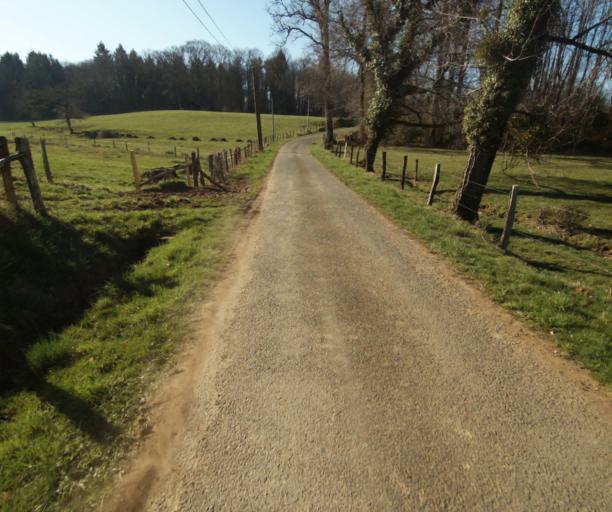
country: FR
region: Limousin
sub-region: Departement de la Correze
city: Saint-Clement
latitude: 45.3797
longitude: 1.6543
